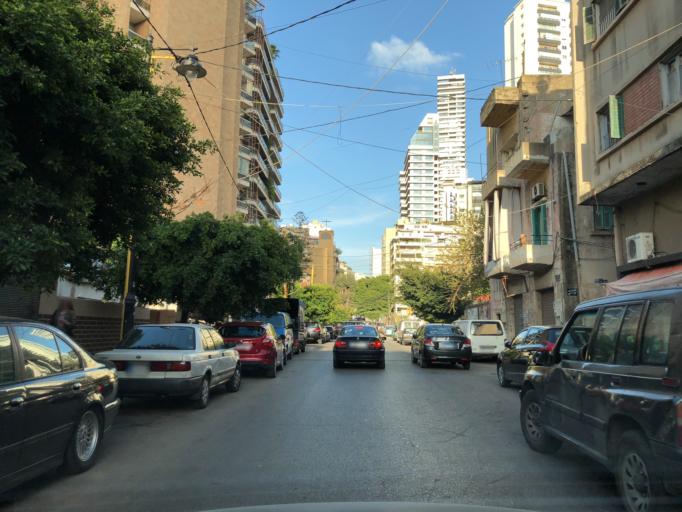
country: LB
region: Beyrouth
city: Beirut
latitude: 33.8873
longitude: 35.5124
